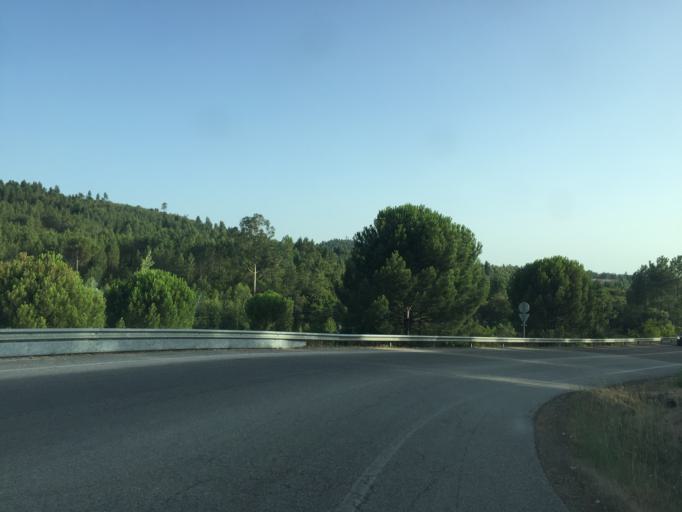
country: PT
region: Santarem
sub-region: Entroncamento
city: Entroncamento
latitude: 39.4934
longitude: -8.4412
